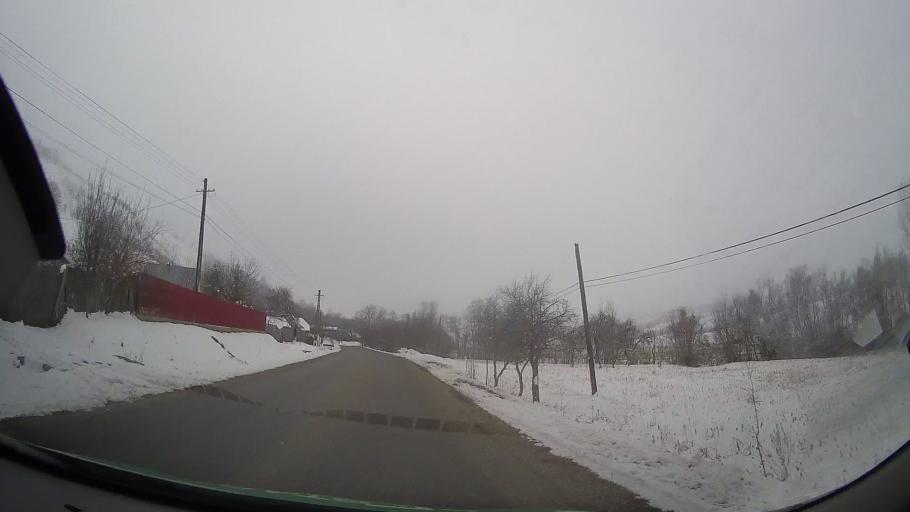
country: RO
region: Bacau
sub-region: Comuna Vultureni
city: Vultureni
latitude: 46.3893
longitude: 27.2790
